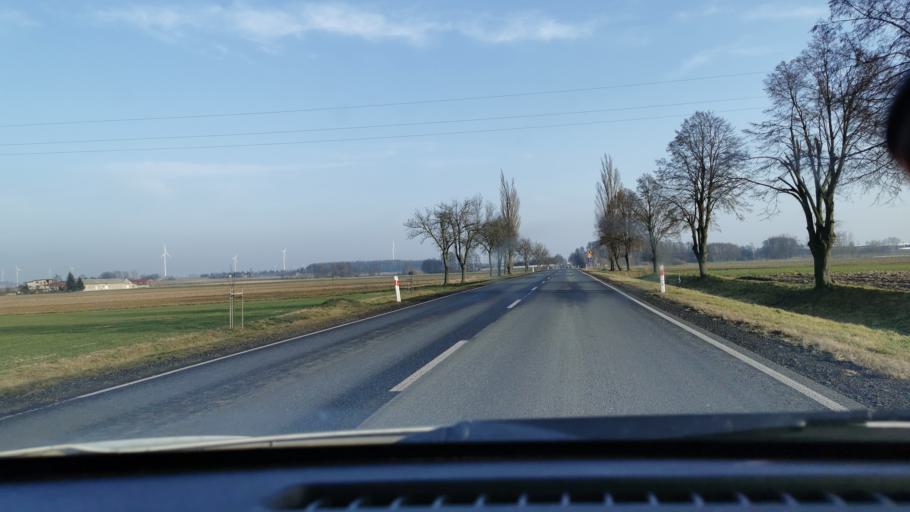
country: PL
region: Lodz Voivodeship
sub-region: Powiat sieradzki
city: Blaszki
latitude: 51.6428
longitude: 18.4884
